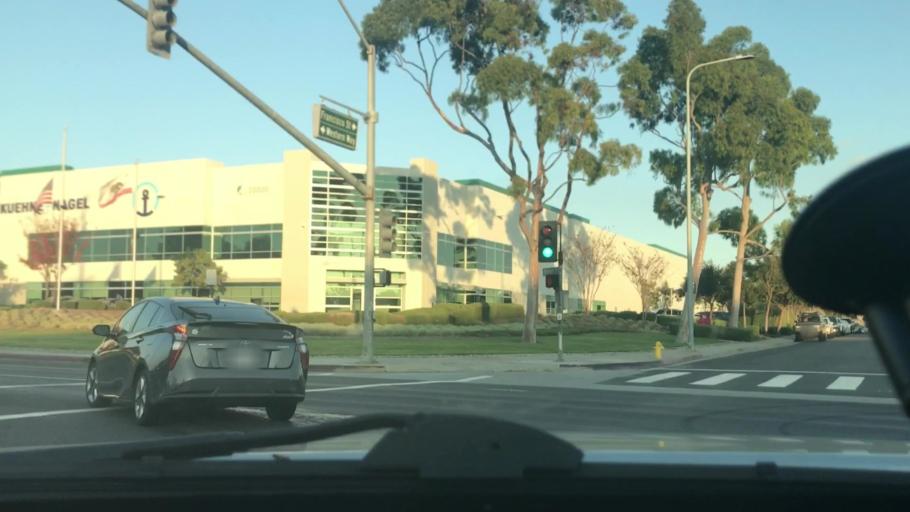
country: US
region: California
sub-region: Los Angeles County
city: West Carson
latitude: 33.8496
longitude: -118.3093
